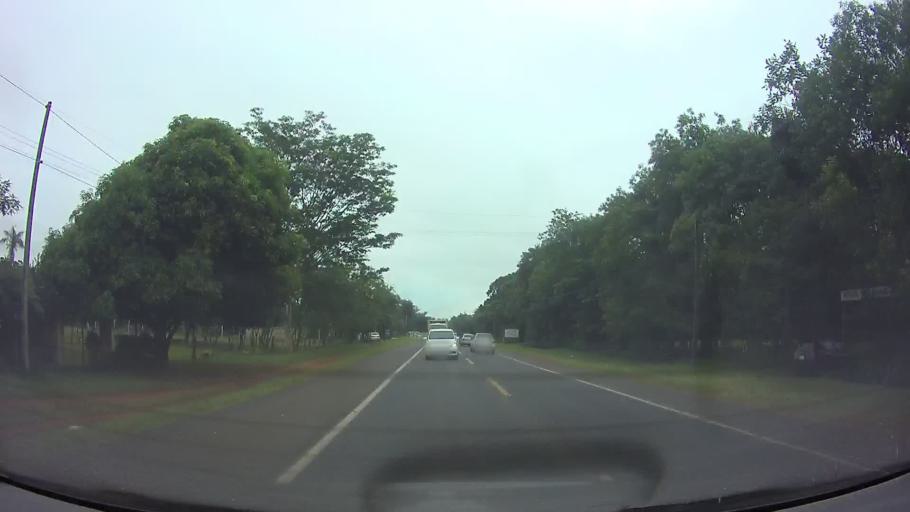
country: PY
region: Paraguari
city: Paraguari
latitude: -25.5972
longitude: -57.2096
